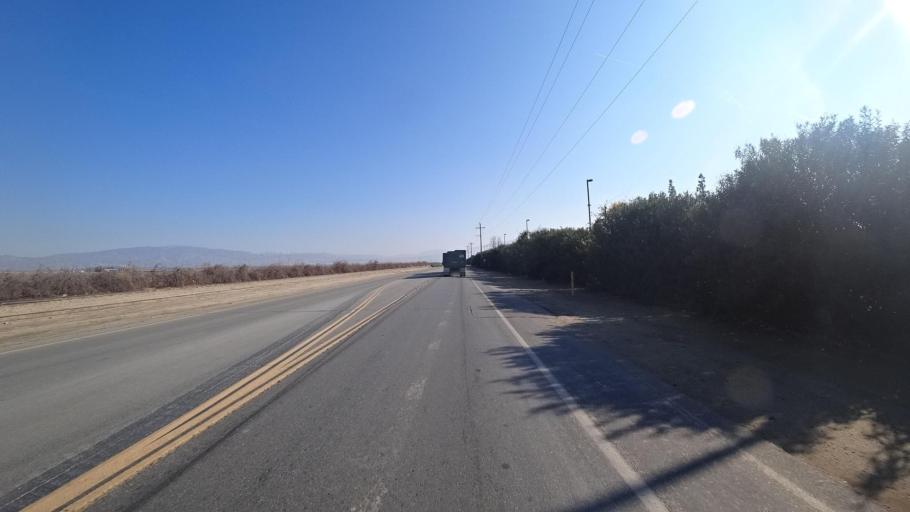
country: US
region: California
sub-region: Kern County
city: Lamont
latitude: 35.2526
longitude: -118.8685
